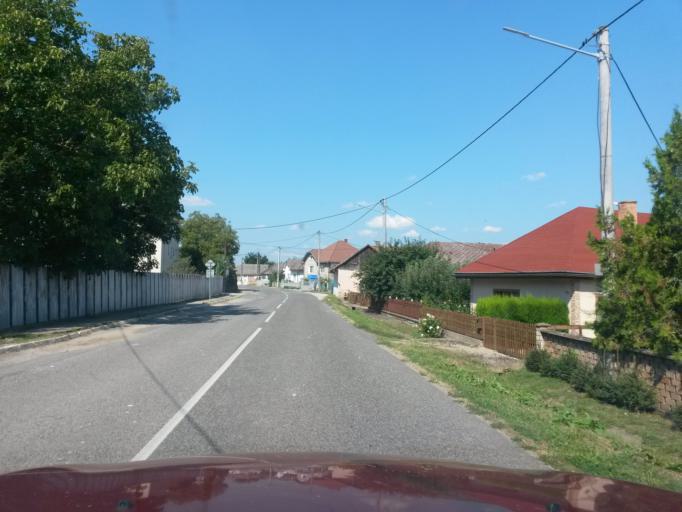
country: SK
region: Kosicky
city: Moldava nad Bodvou
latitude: 48.5343
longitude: 21.0795
